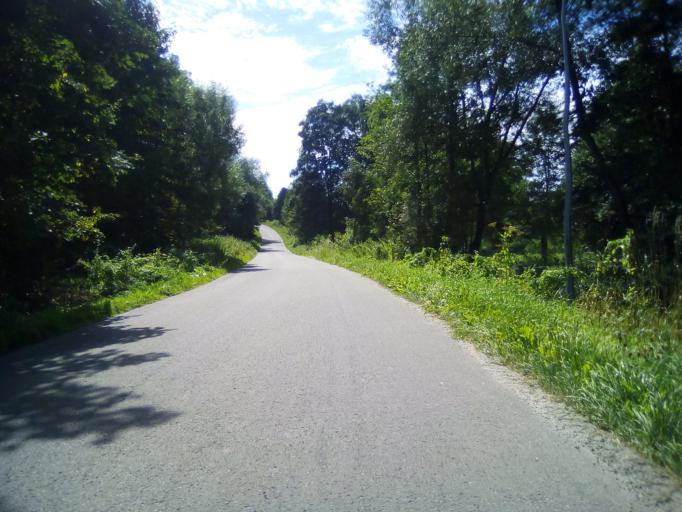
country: PL
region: Subcarpathian Voivodeship
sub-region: Powiat strzyzowski
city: Konieczkowa
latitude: 49.8280
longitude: 21.9282
